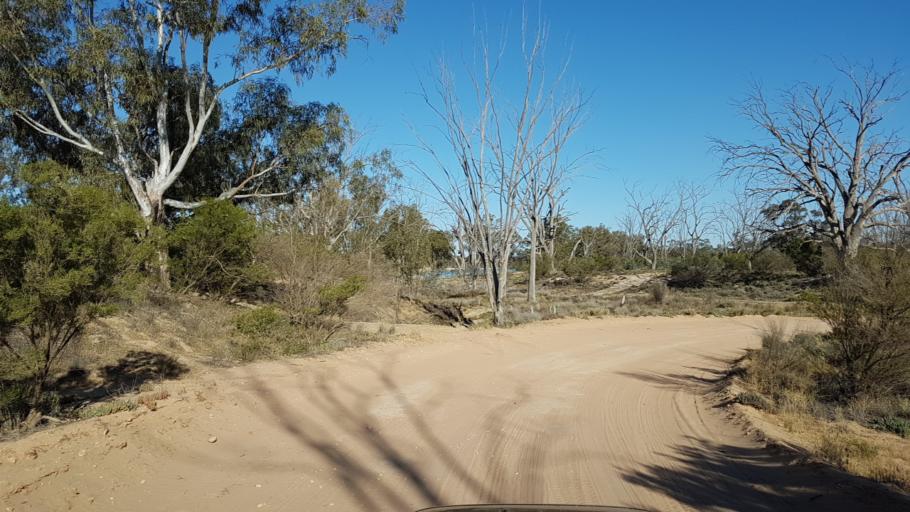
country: AU
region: South Australia
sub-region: Loxton Waikerie
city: Waikerie
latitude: -34.1572
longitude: 140.0247
